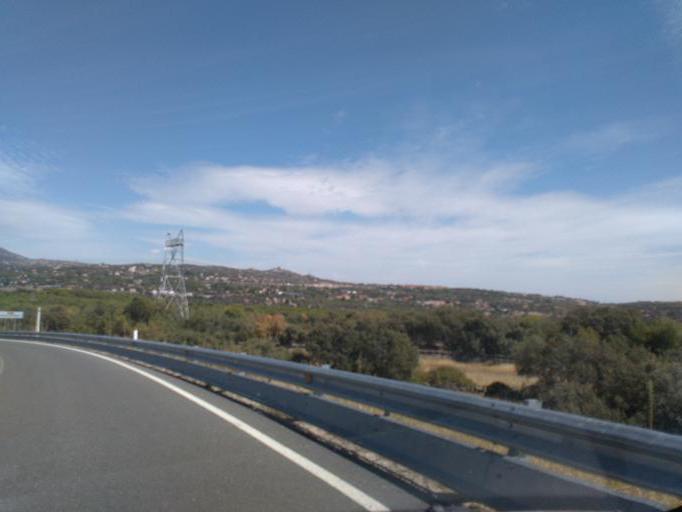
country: ES
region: Madrid
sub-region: Provincia de Madrid
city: Galapagar
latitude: 40.5696
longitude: -3.9767
